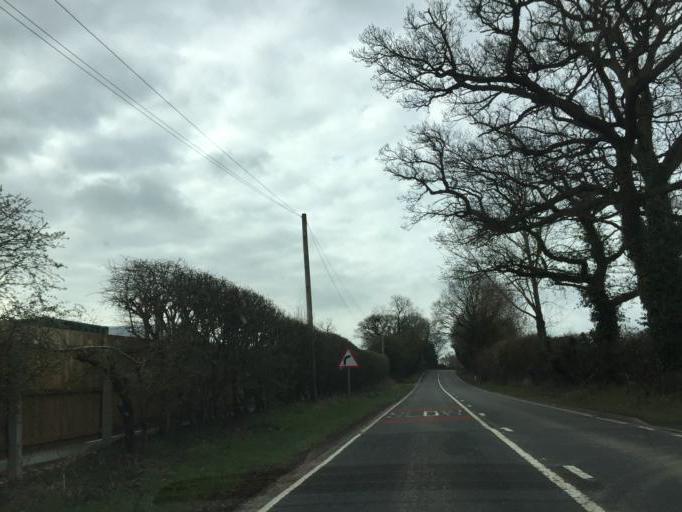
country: GB
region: England
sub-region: Warwickshire
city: Studley
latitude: 52.3001
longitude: -1.8396
